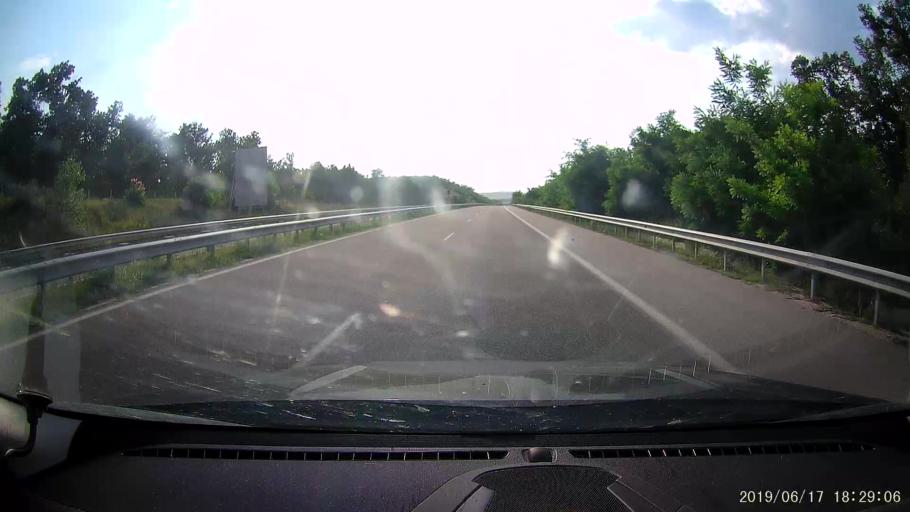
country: BG
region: Khaskovo
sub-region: Obshtina Dimitrovgrad
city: Dimitrovgrad
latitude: 42.0264
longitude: 25.5634
